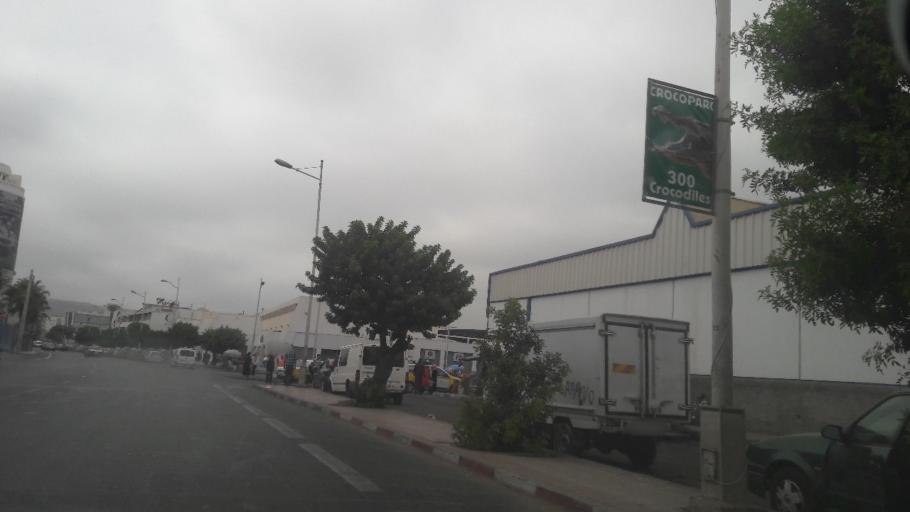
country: MA
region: Souss-Massa-Draa
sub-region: Agadir-Ida-ou-Tnan
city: Agadir
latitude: 30.4093
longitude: -9.5889
